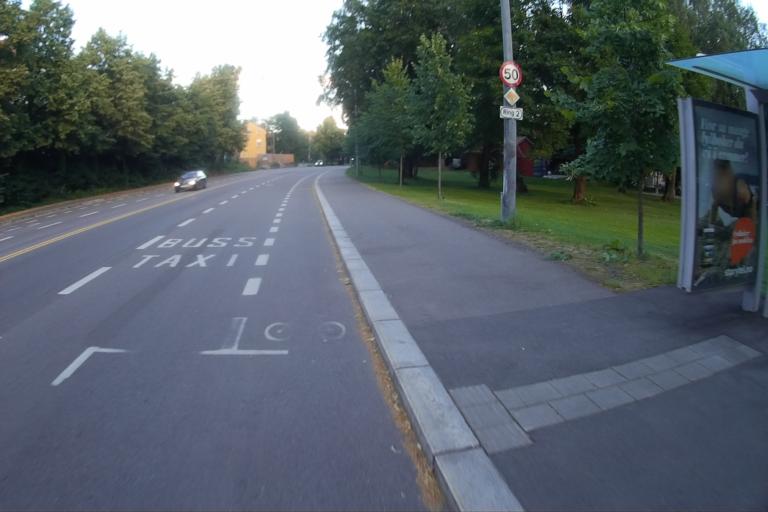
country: NO
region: Oslo
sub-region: Oslo
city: Oslo
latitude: 59.9317
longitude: 10.7631
